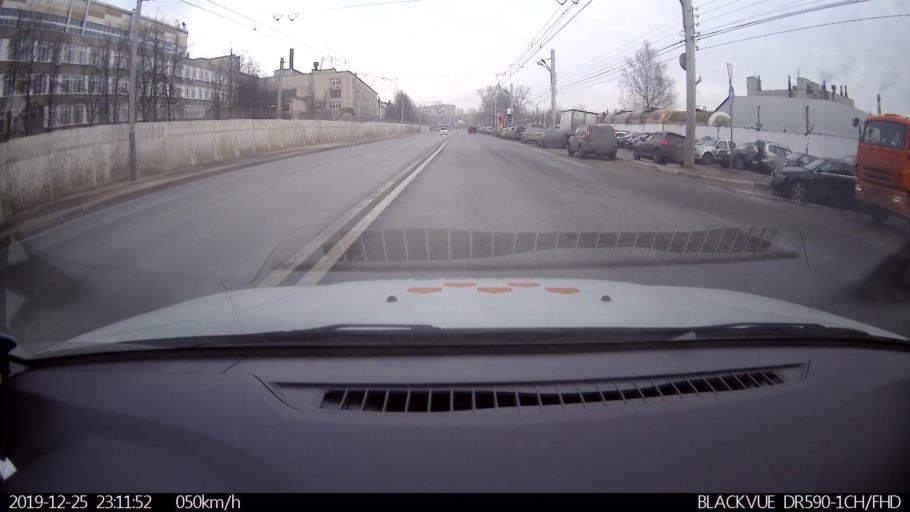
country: RU
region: Nizjnij Novgorod
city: Nizhniy Novgorod
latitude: 56.3212
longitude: 43.9084
